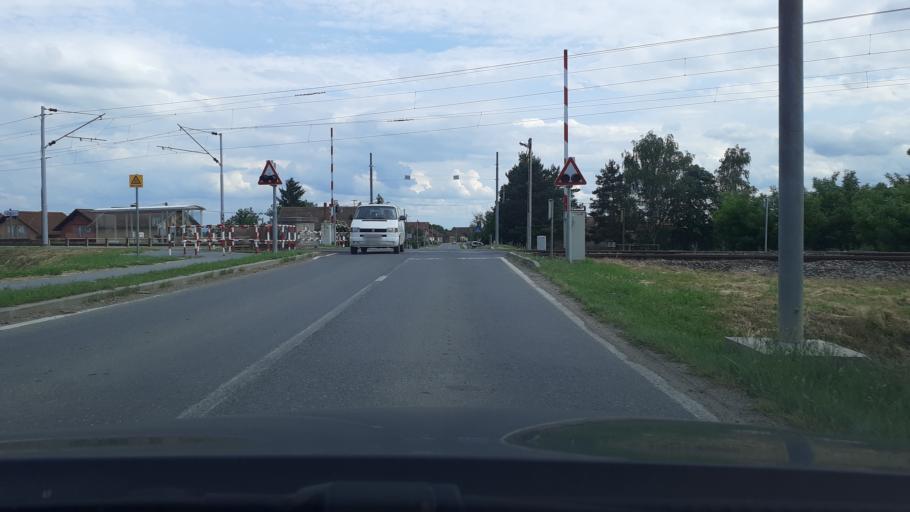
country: HR
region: Brodsko-Posavska
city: Slobodnica
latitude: 45.1773
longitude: 17.9271
